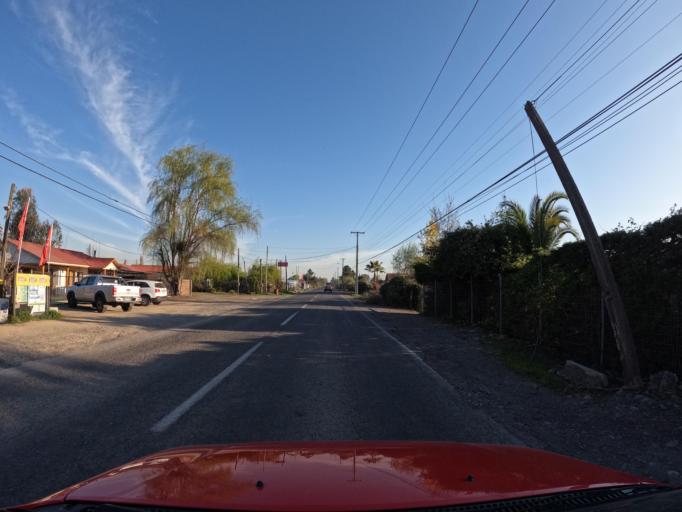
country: CL
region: Maule
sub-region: Provincia de Curico
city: Rauco
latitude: -34.8725
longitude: -71.2663
